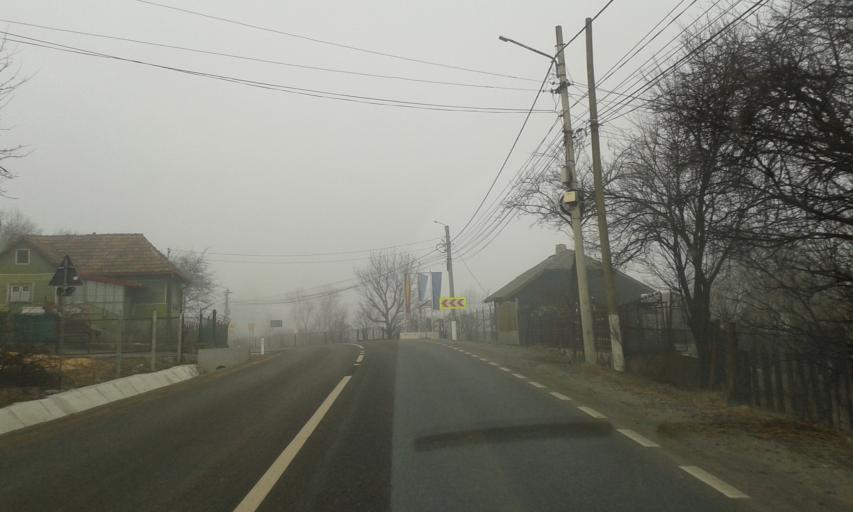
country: RO
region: Hunedoara
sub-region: Comuna Aninoasa
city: Iscroni
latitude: 45.3785
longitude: 23.3222
